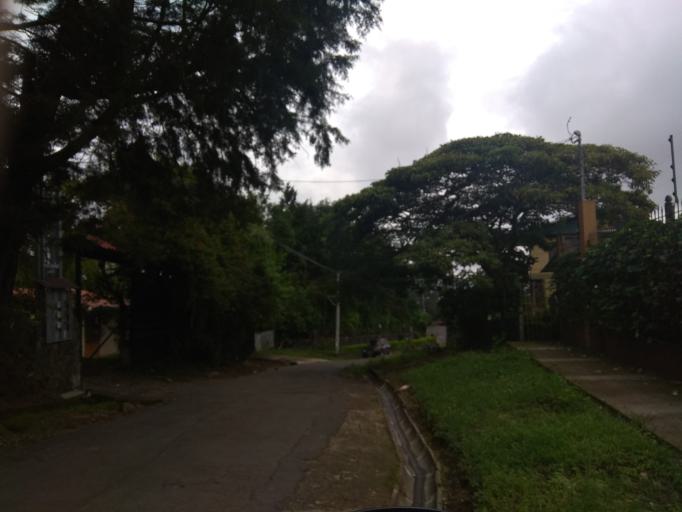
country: CR
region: Heredia
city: San Josecito
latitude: 10.0379
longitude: -84.0984
